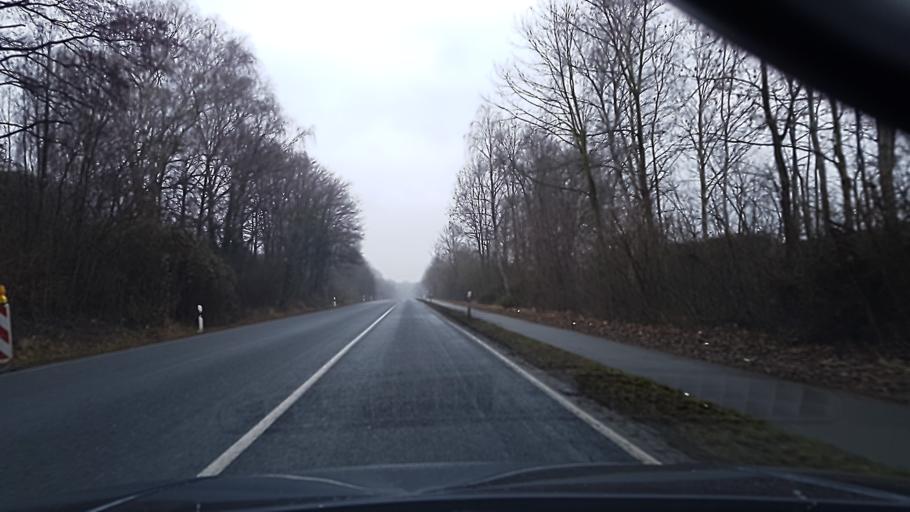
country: DE
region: Lower Saxony
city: Leiferde
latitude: 52.1903
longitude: 10.4568
